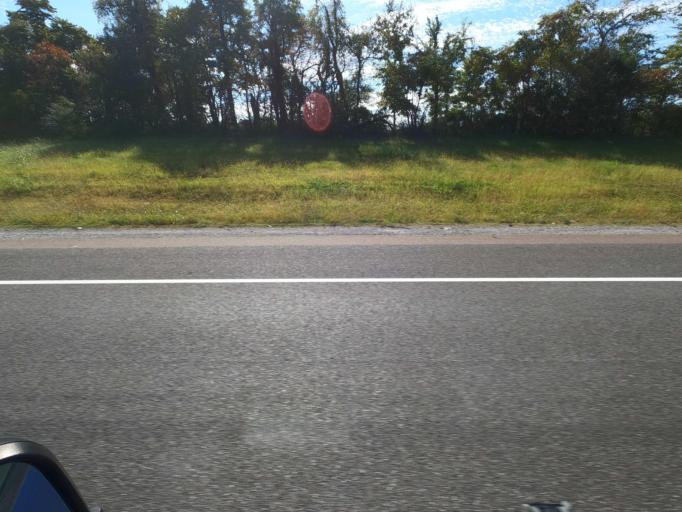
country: US
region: Tennessee
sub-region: Haywood County
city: Brownsville
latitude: 35.5390
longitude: -89.2443
